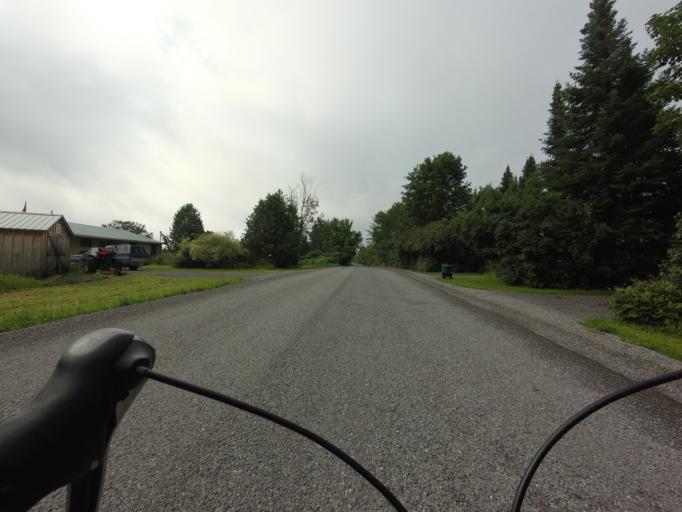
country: CA
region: Ontario
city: Bells Corners
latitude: 45.0826
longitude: -75.7573
